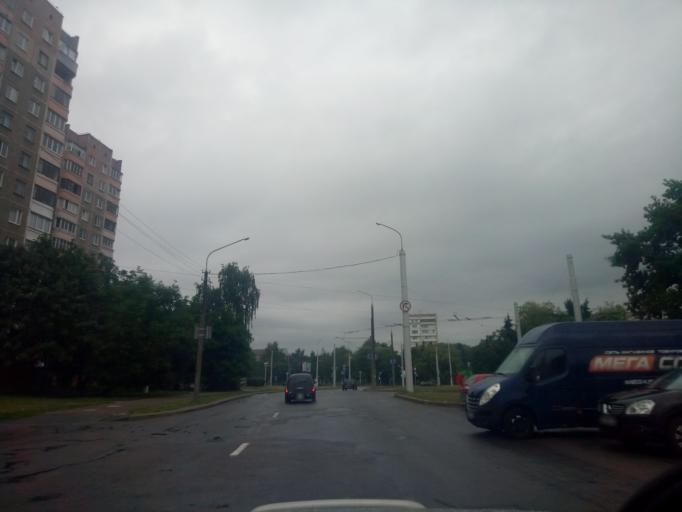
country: BY
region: Minsk
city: Novoye Medvezhino
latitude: 53.9085
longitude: 27.5004
